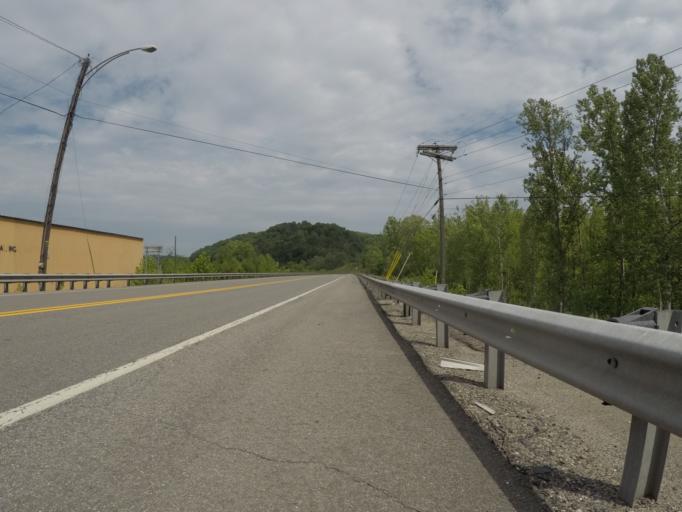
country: US
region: West Virginia
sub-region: Wayne County
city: Kenova
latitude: 38.3353
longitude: -82.5805
